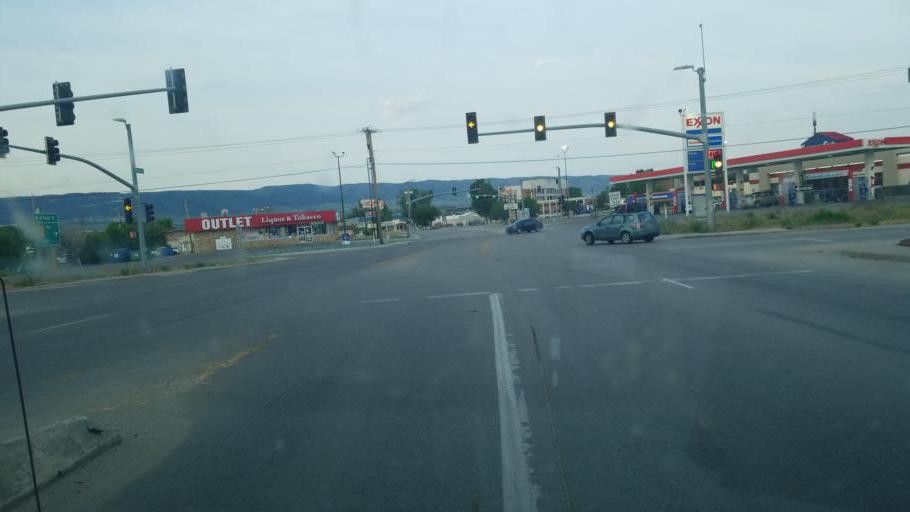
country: US
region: Wyoming
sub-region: Natrona County
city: Casper
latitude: 42.8575
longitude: -106.3338
